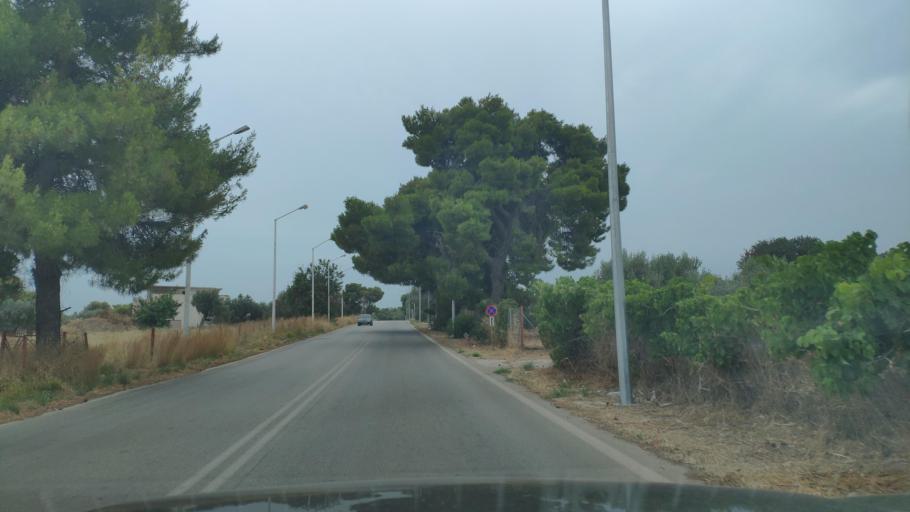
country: GR
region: Peloponnese
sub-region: Nomos Argolidos
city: Porto Cheli
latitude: 37.3409
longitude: 23.1569
